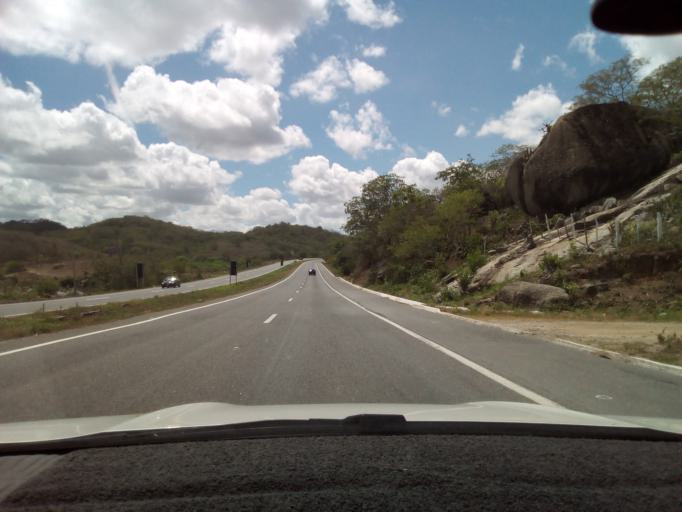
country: BR
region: Paraiba
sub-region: Massaranduba
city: Massaranduba
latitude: -7.2761
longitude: -35.7801
